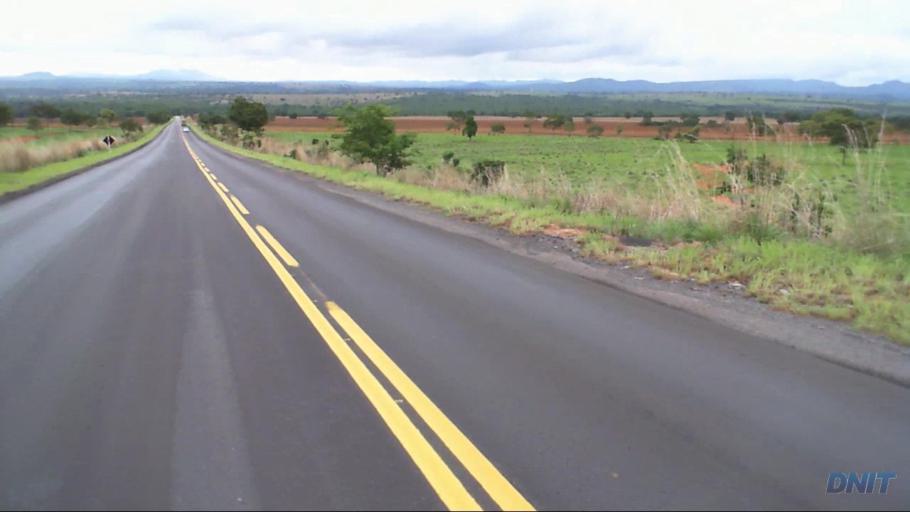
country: BR
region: Goias
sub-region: Padre Bernardo
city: Padre Bernardo
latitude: -15.2200
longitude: -48.5326
